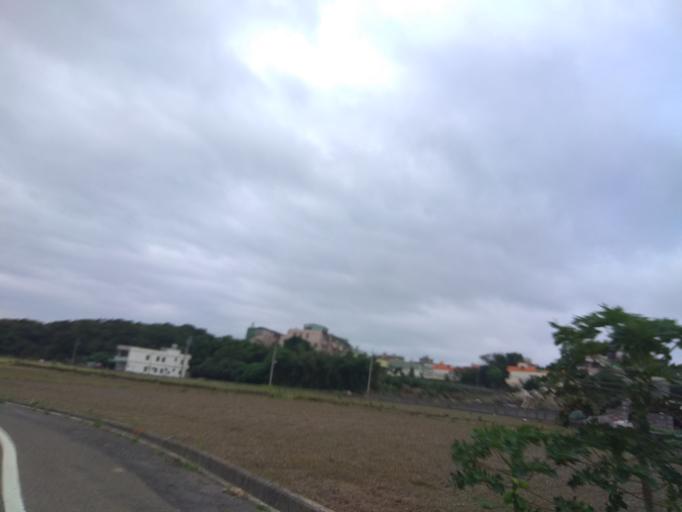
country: TW
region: Taiwan
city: Taoyuan City
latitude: 25.0311
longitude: 121.2206
